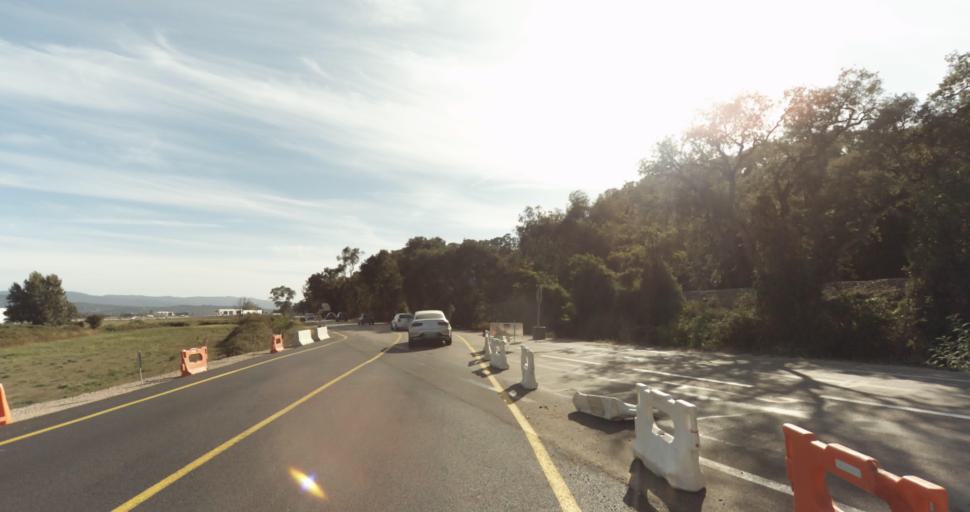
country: FR
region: Corsica
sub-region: Departement de la Corse-du-Sud
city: Afa
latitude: 41.9366
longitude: 8.8035
